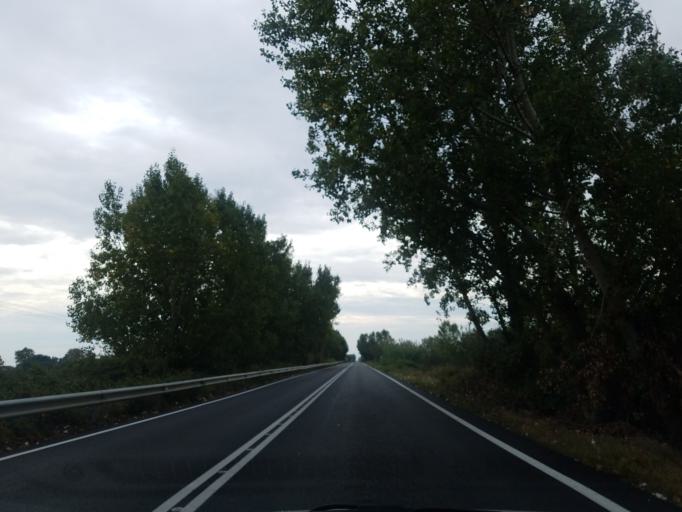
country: GR
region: Thessaly
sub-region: Nomos Kardhitsas
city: Agnantero
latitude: 39.4610
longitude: 21.8545
